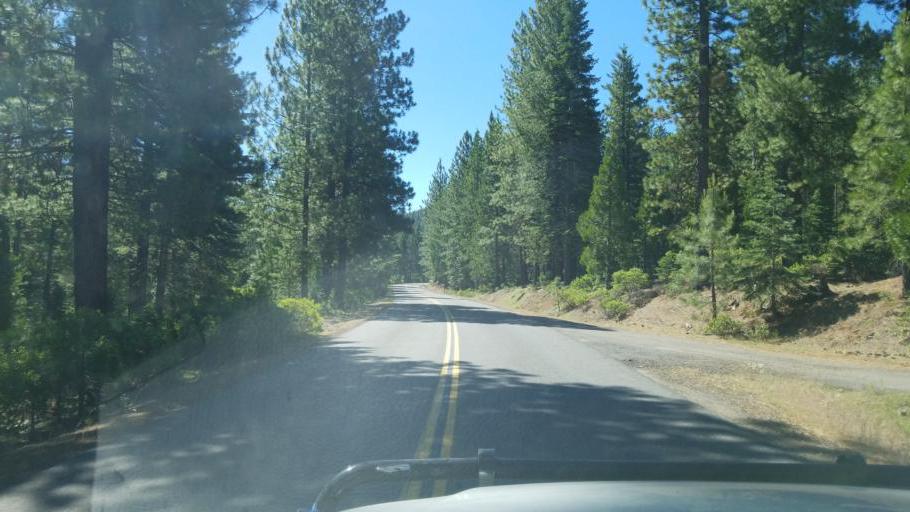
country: US
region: California
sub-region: Lassen County
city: Susanville
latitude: 40.5163
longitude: -120.7826
